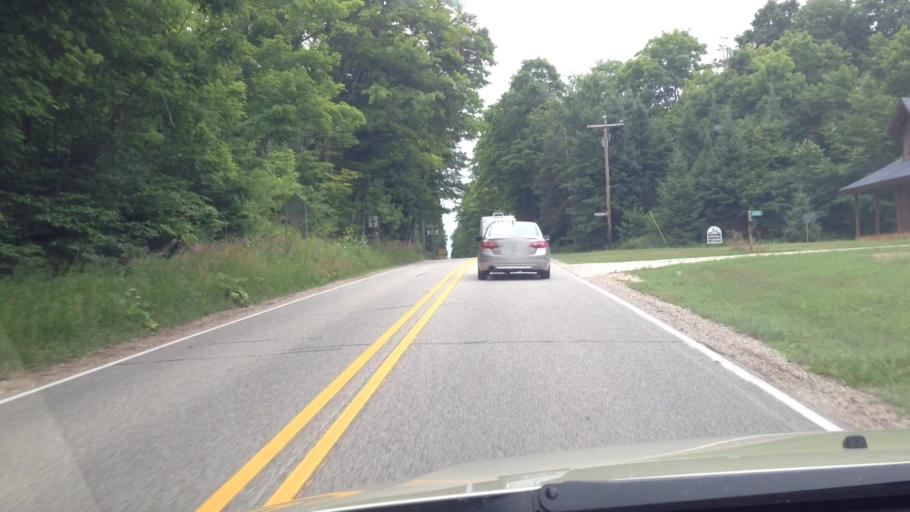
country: US
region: Michigan
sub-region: Mackinac County
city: Saint Ignace
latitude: 46.0506
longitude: -85.1070
